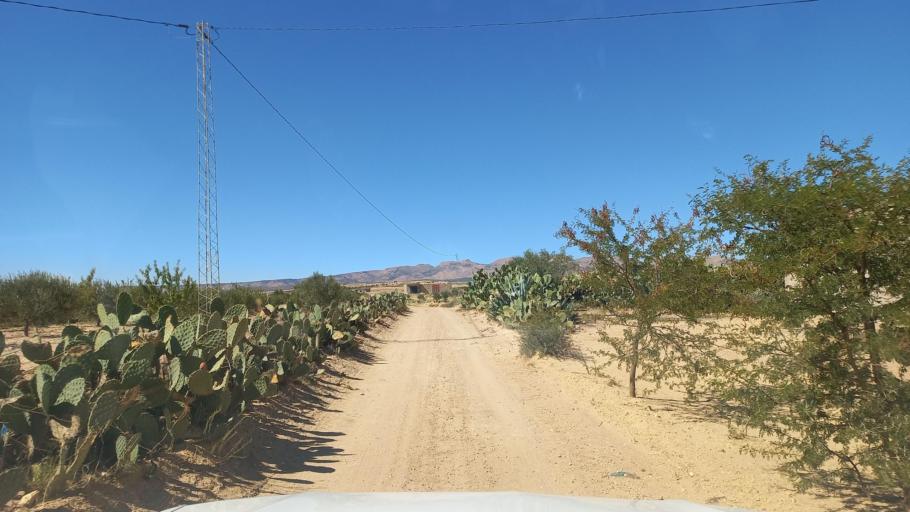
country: TN
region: Al Qasrayn
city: Sbiba
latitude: 35.3654
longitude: 9.0892
